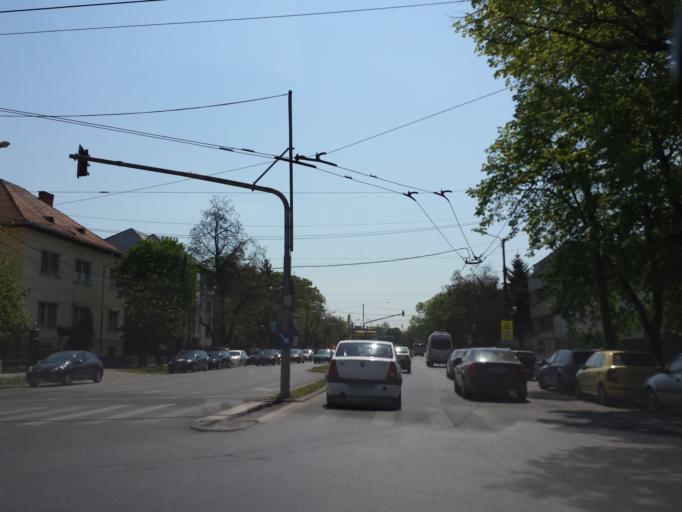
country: RO
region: Timis
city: Timisoara
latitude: 45.7526
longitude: 21.2326
